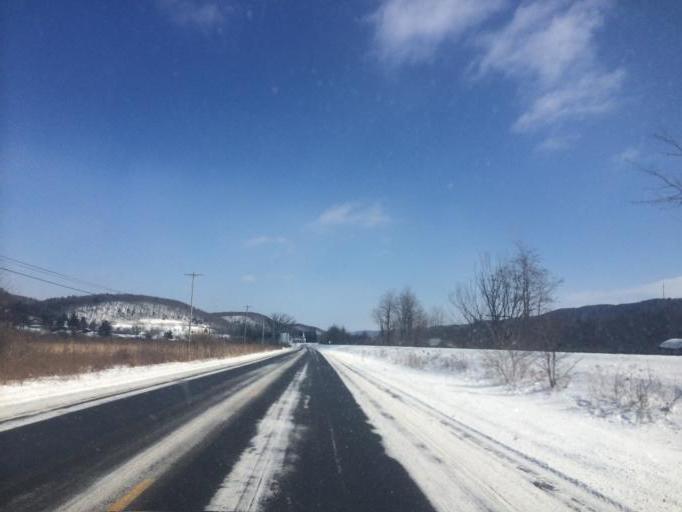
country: US
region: Pennsylvania
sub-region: Centre County
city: Stormstown
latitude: 40.8345
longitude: -78.0057
